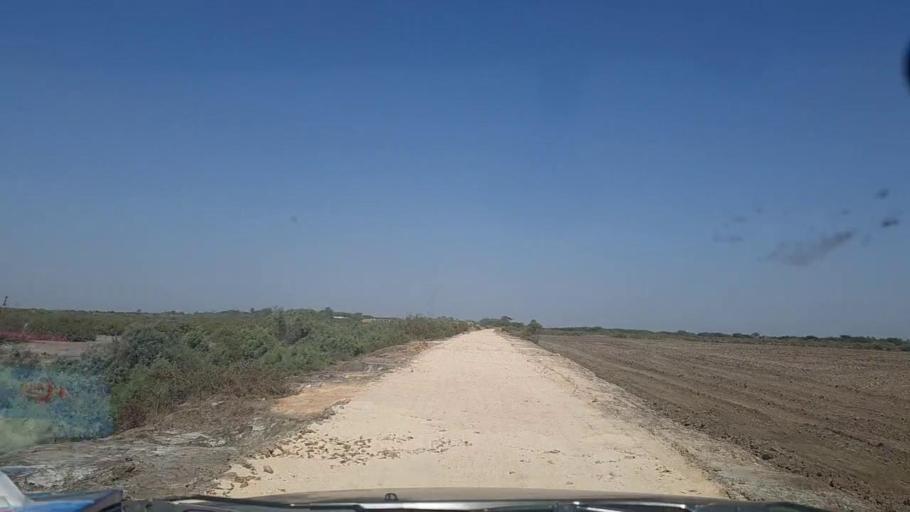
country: PK
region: Sindh
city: Chuhar Jamali
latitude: 24.2703
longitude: 67.7459
